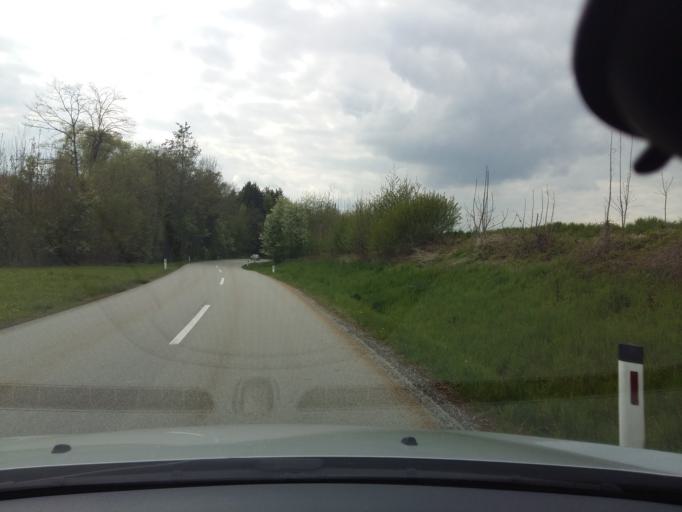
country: AT
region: Upper Austria
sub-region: Politischer Bezirk Scharding
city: Sankt Marienkirchen bei Schaerding
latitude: 48.3810
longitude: 13.4358
